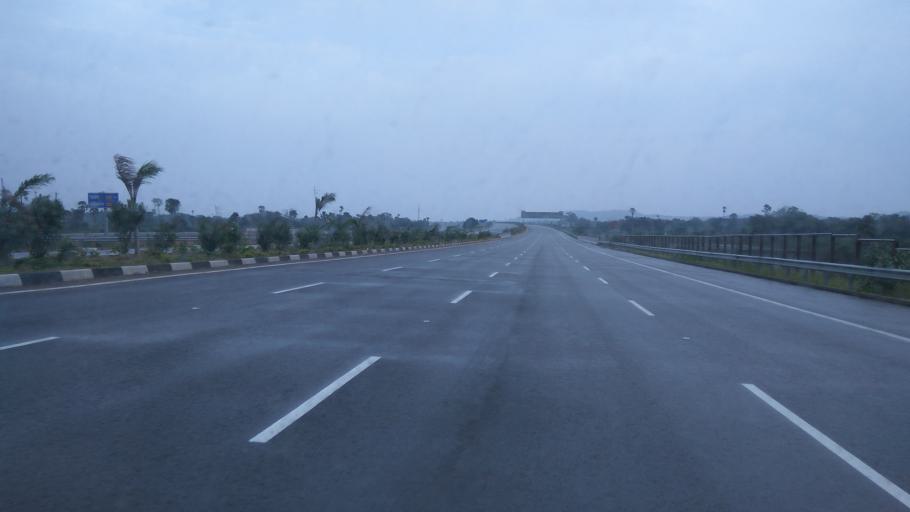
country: IN
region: Telangana
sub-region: Rangareddi
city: Ghatkesar
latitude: 17.4577
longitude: 78.6696
